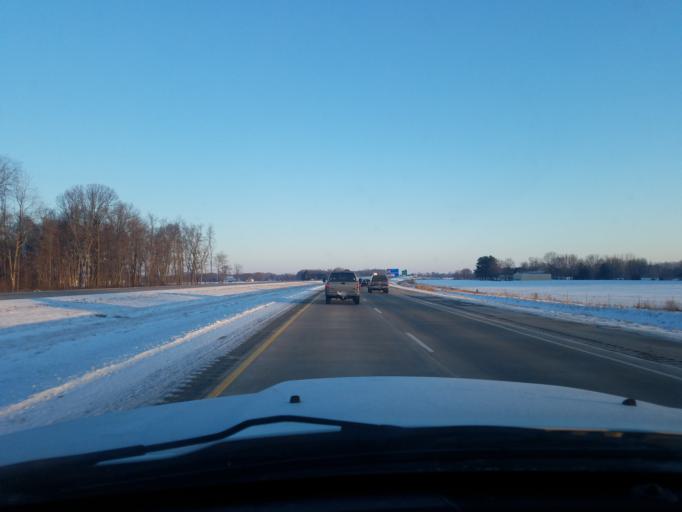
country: US
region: Indiana
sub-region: Marshall County
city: Plymouth
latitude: 41.4250
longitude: -86.2981
